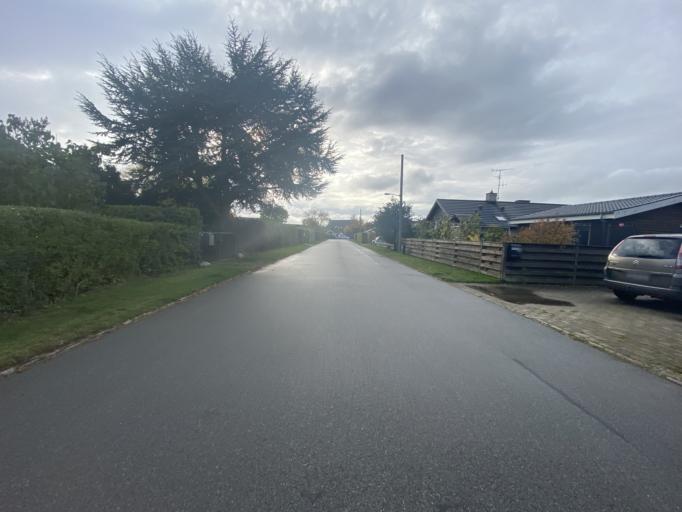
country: DK
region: Capital Region
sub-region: Dragor Kommune
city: Dragor
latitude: 55.5859
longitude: 12.6474
